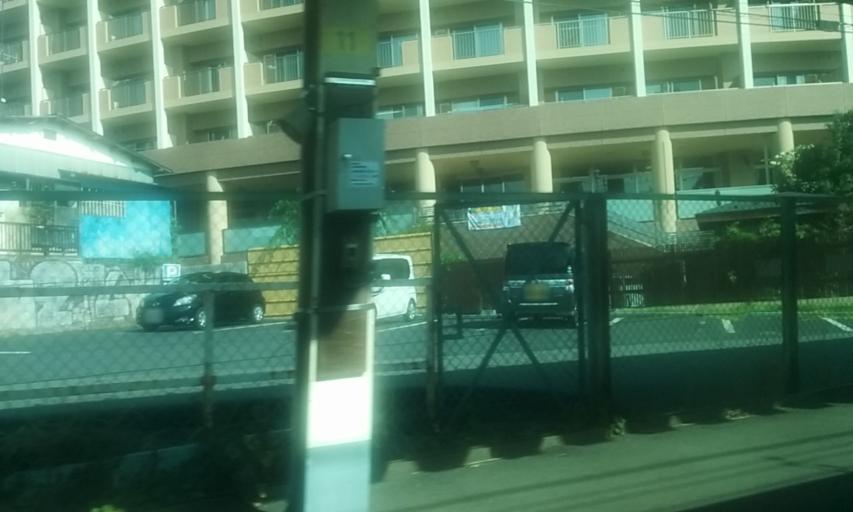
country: JP
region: Saitama
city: Hasuda
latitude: 35.9799
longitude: 139.6522
